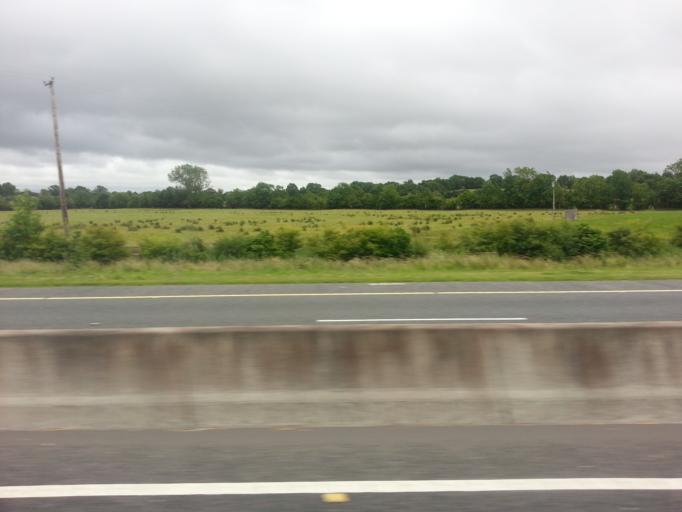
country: IE
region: Leinster
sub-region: Kildare
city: Castledermot
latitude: 52.8459
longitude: -6.8419
